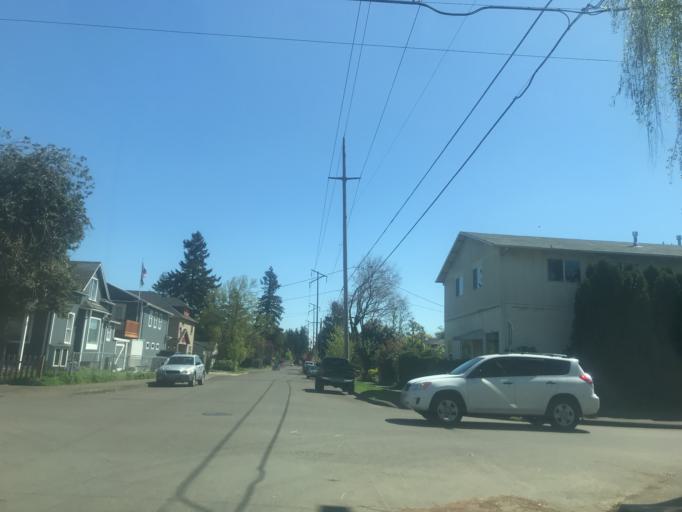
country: US
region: Oregon
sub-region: Multnomah County
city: Lents
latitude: 45.4818
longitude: -122.5972
